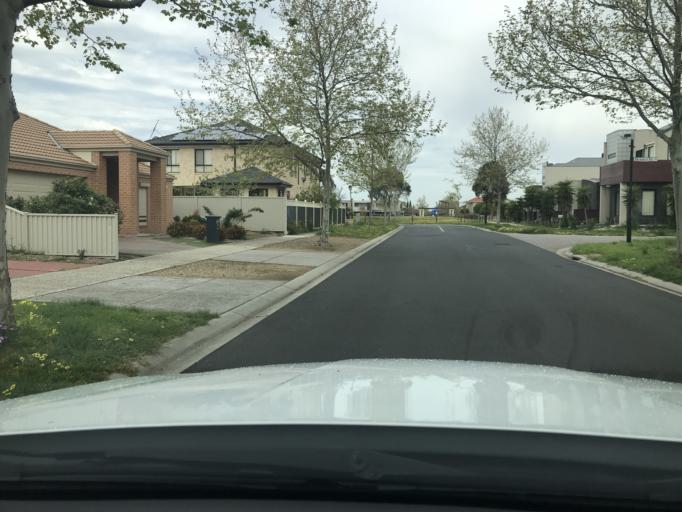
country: AU
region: Victoria
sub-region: Hume
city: Roxburgh Park
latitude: -37.6025
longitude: 144.9141
